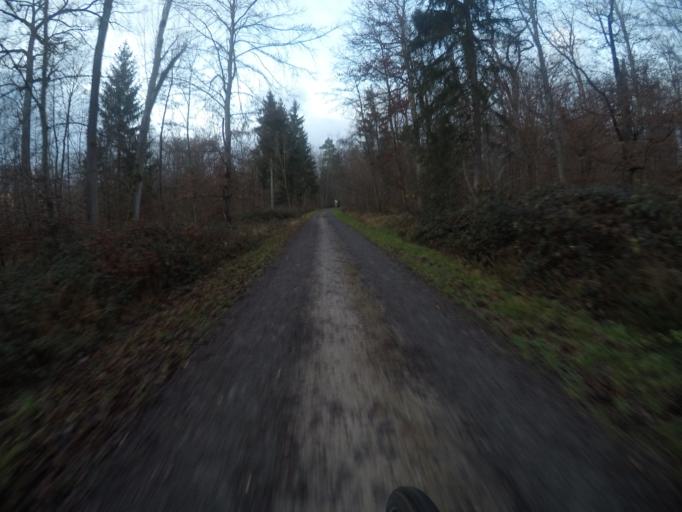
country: DE
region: Baden-Wuerttemberg
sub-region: Tuebingen Region
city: Dettenhausen
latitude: 48.5722
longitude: 9.1068
